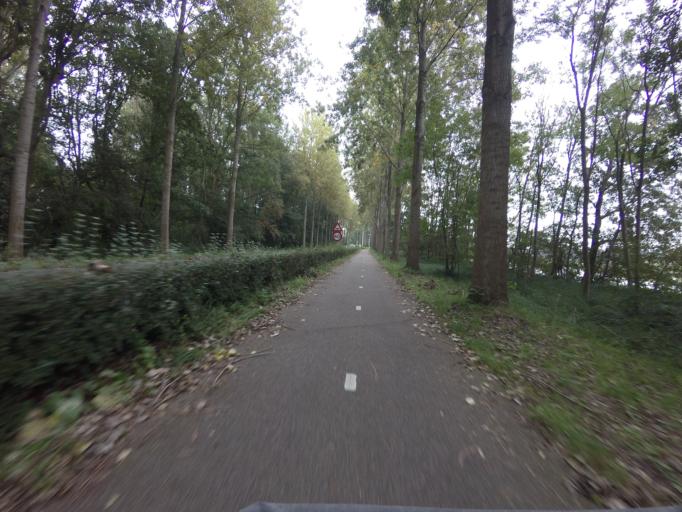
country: NL
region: Utrecht
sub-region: Stichtse Vecht
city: Vreeland
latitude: 52.2018
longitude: 5.0385
